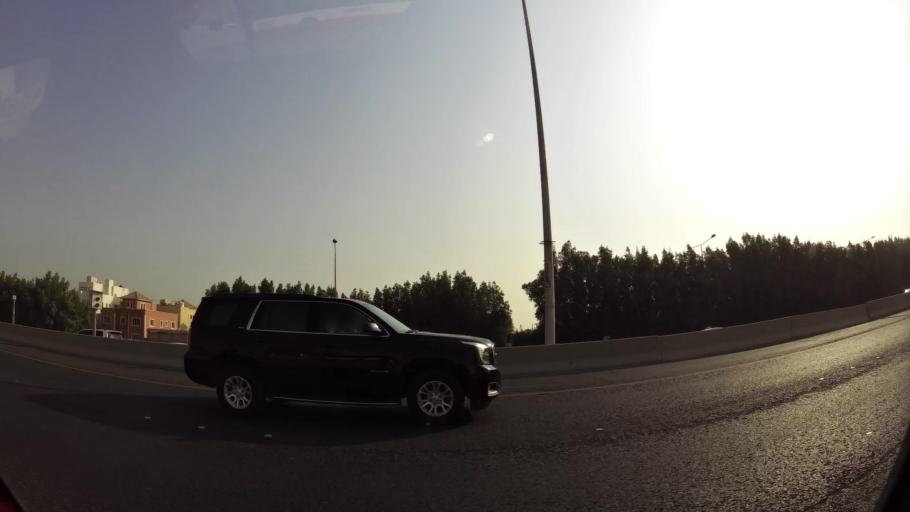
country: KW
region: Mubarak al Kabir
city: Mubarak al Kabir
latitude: 29.1987
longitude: 48.1074
